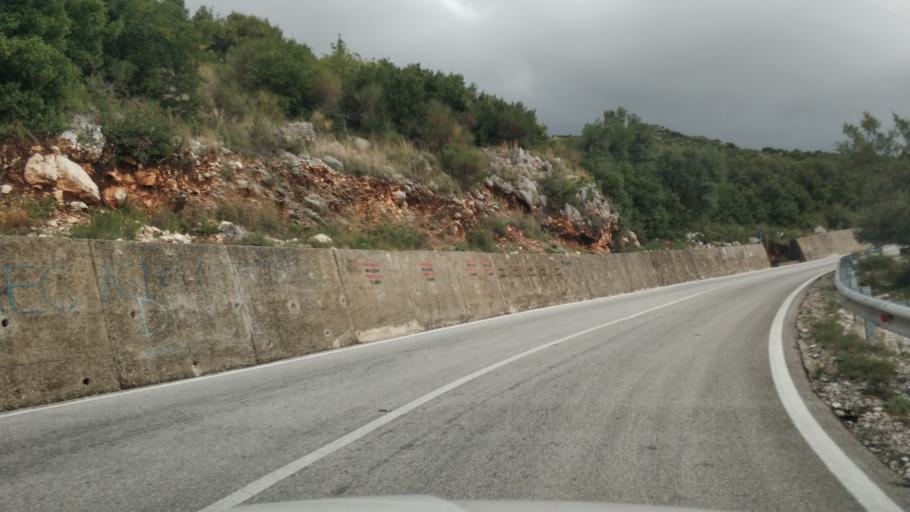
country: AL
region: Vlore
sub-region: Rrethi i Vlores
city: Vranisht
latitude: 40.1596
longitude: 19.6287
